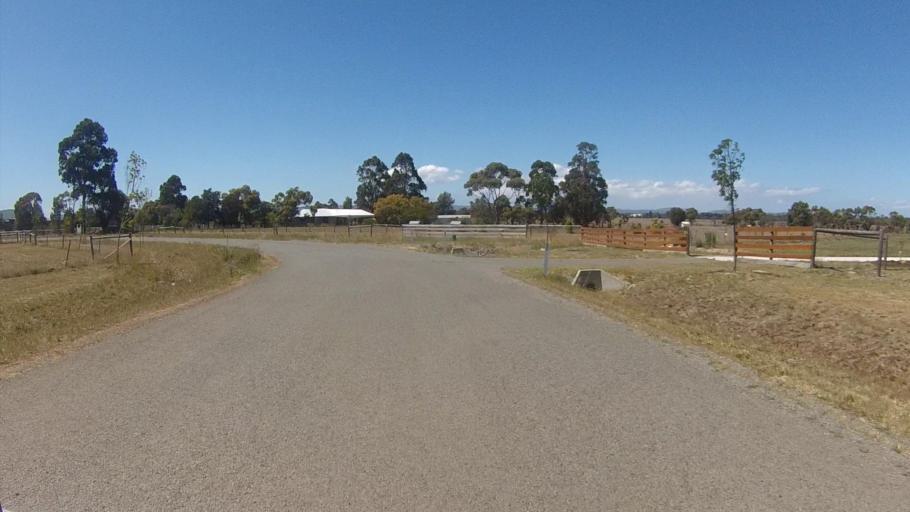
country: AU
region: Tasmania
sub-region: Clarence
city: Seven Mile Beach
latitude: -42.8448
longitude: 147.4817
